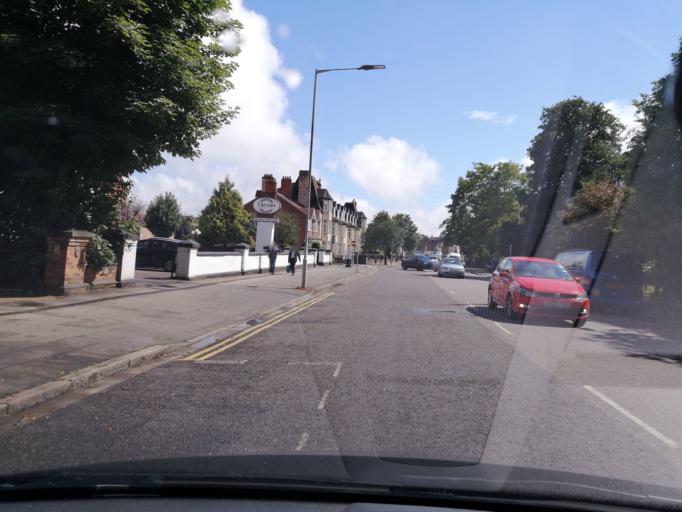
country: GB
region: England
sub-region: Peterborough
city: Peterborough
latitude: 52.5790
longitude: -0.2434
